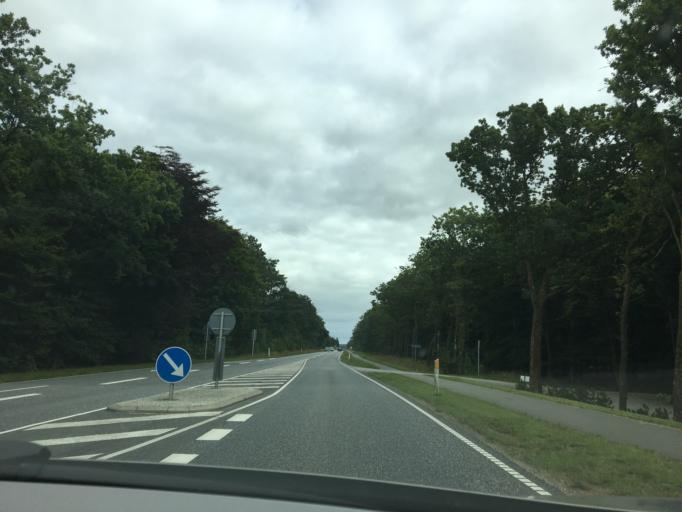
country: DK
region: Central Jutland
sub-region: Ringkobing-Skjern Kommune
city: Ringkobing
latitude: 56.0845
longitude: 8.3172
